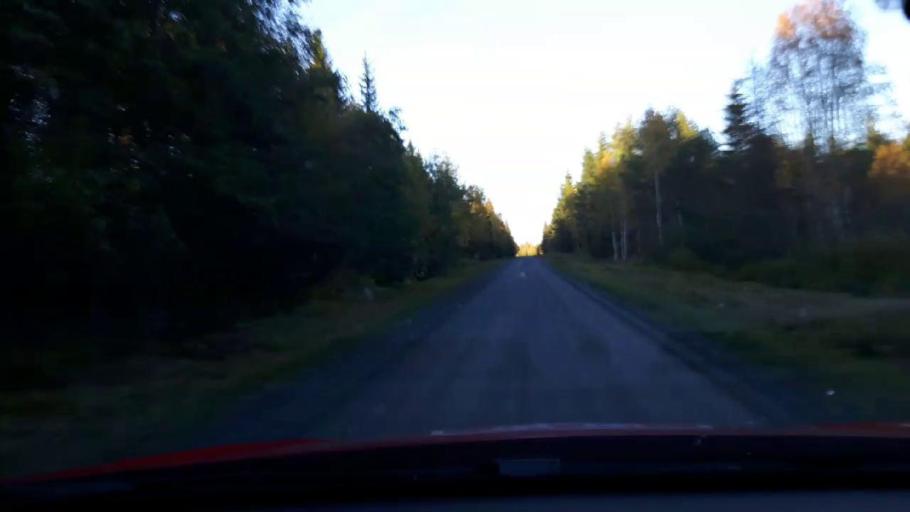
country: SE
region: Jaemtland
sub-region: Krokoms Kommun
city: Krokom
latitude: 63.4229
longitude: 14.6079
